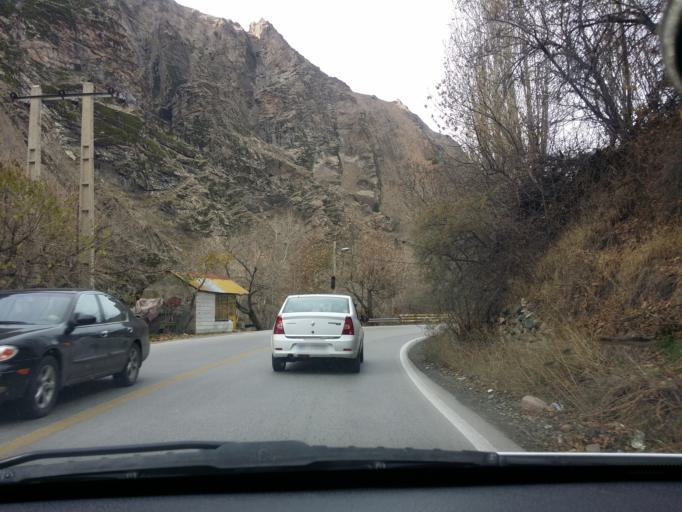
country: IR
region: Tehran
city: Tajrish
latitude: 36.0225
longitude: 51.2618
